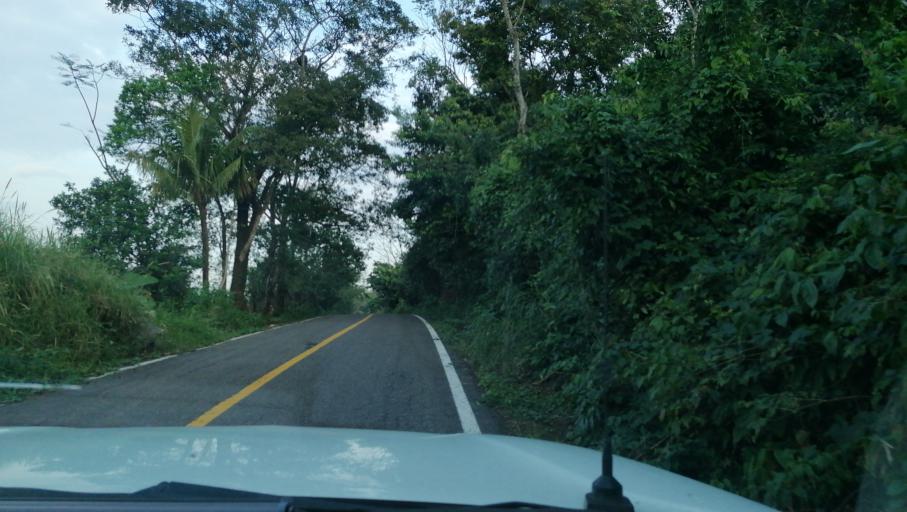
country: MX
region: Chiapas
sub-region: Juarez
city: El Triunfo 1ra. Seccion (Cardona)
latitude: 17.5056
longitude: -93.2251
